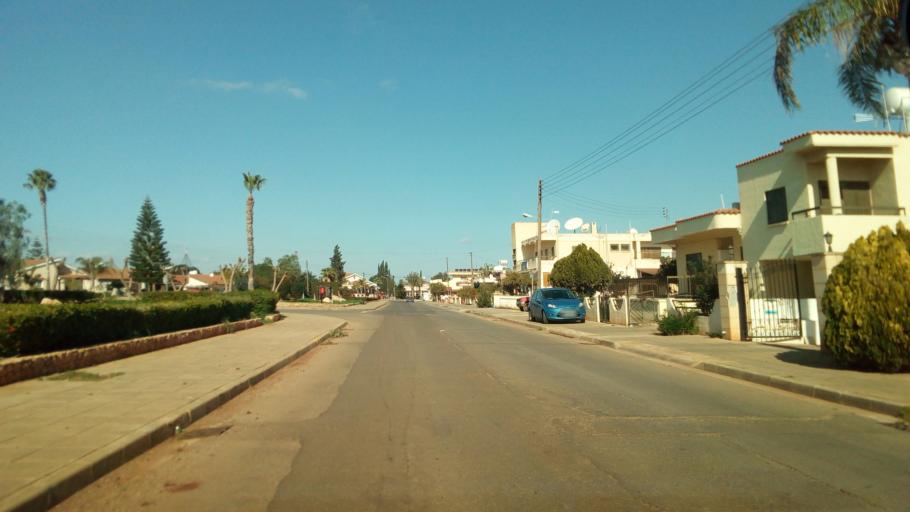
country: CY
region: Ammochostos
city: Avgorou
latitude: 35.0269
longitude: 33.8396
